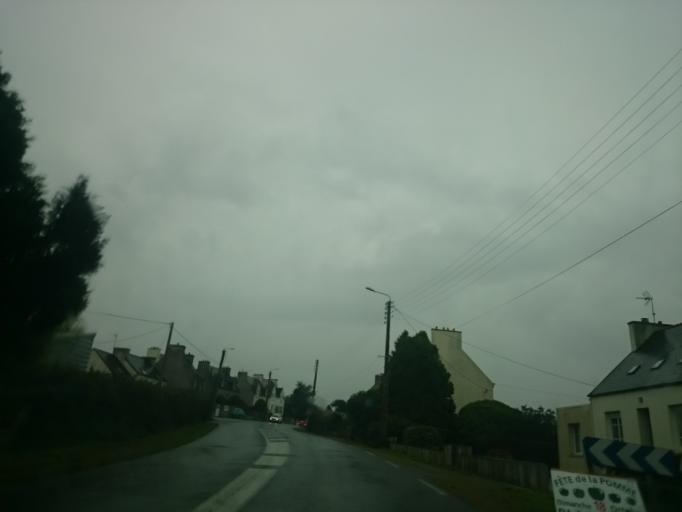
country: FR
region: Brittany
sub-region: Departement du Finistere
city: Le Drennec
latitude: 48.5365
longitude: -4.3718
